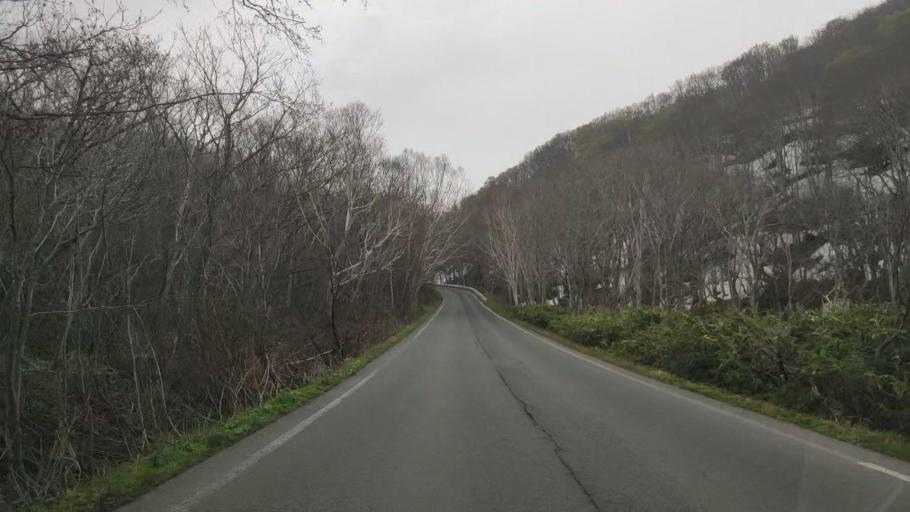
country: JP
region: Aomori
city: Aomori Shi
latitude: 40.6920
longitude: 140.9110
